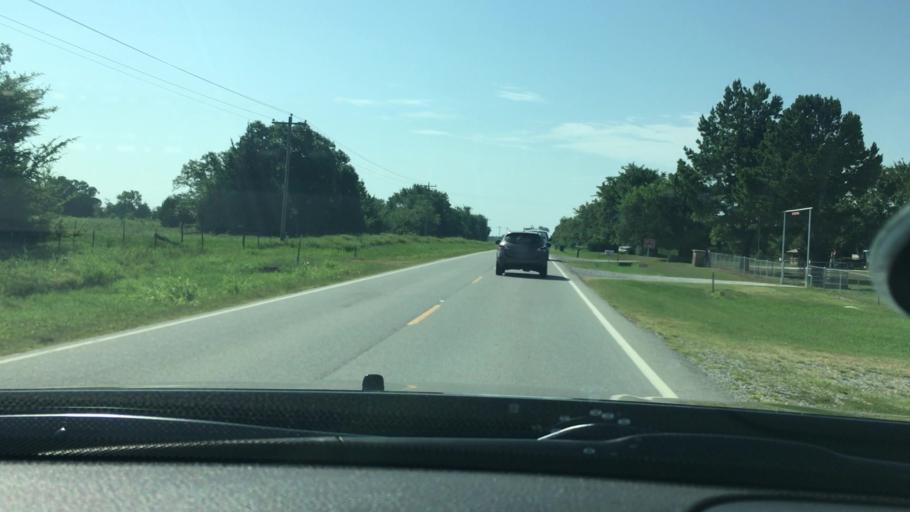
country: US
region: Oklahoma
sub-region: Coal County
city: Coalgate
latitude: 34.5842
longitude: -96.4140
